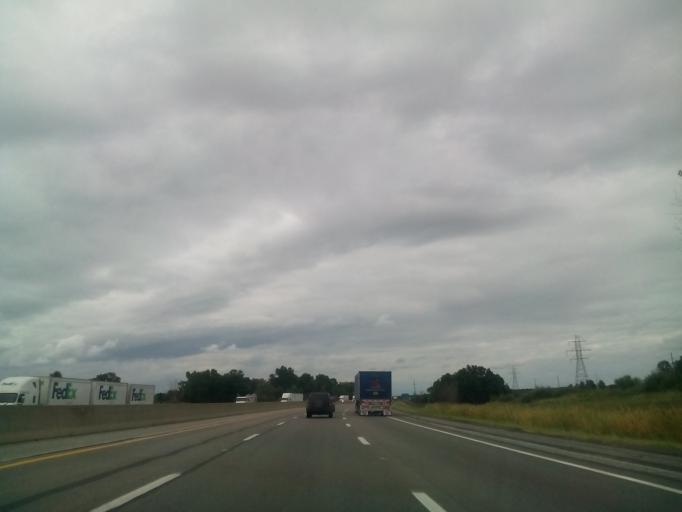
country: US
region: Ohio
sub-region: Lorain County
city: South Amherst
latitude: 41.3764
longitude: -82.2592
